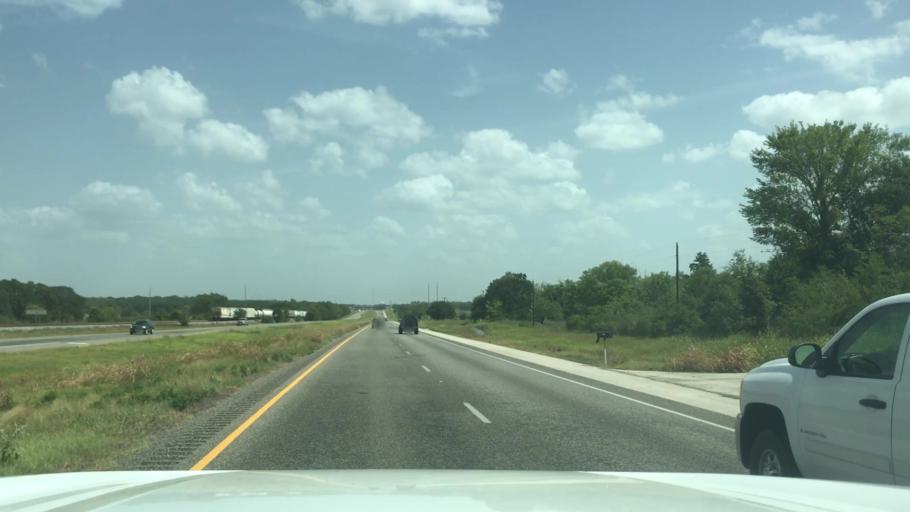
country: US
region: Texas
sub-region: Robertson County
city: Hearne
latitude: 30.9215
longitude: -96.6238
